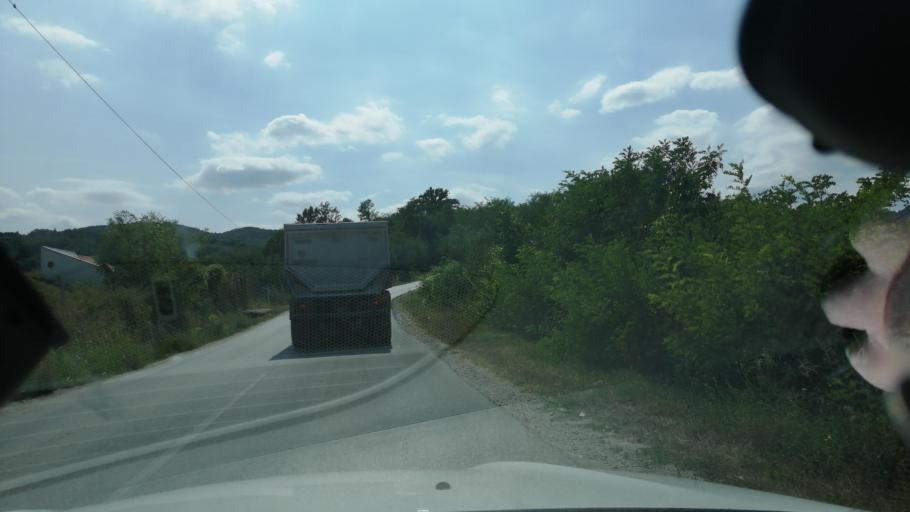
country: RS
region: Central Serbia
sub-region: Moravicki Okrug
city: Cacak
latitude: 43.8558
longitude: 20.3079
